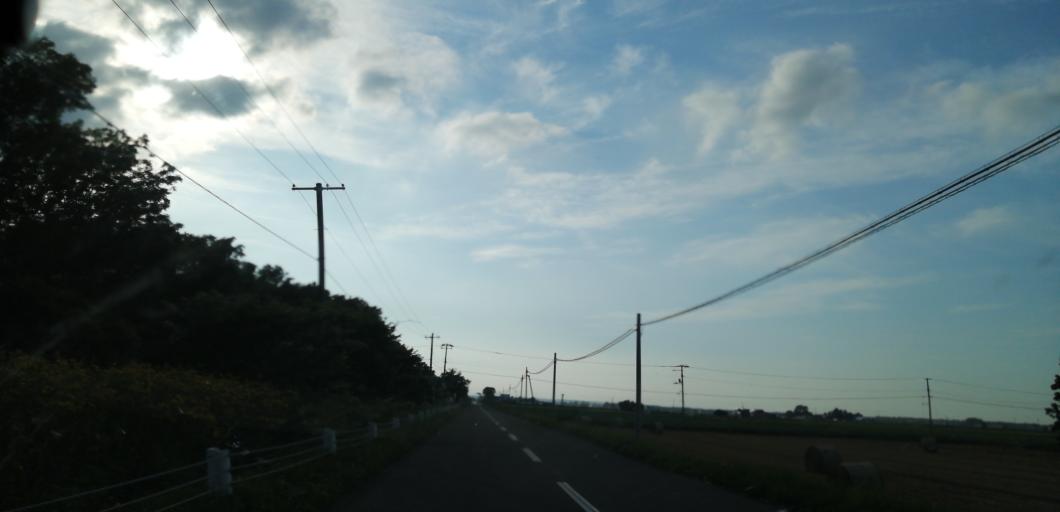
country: JP
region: Hokkaido
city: Chitose
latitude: 42.9415
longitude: 141.6943
